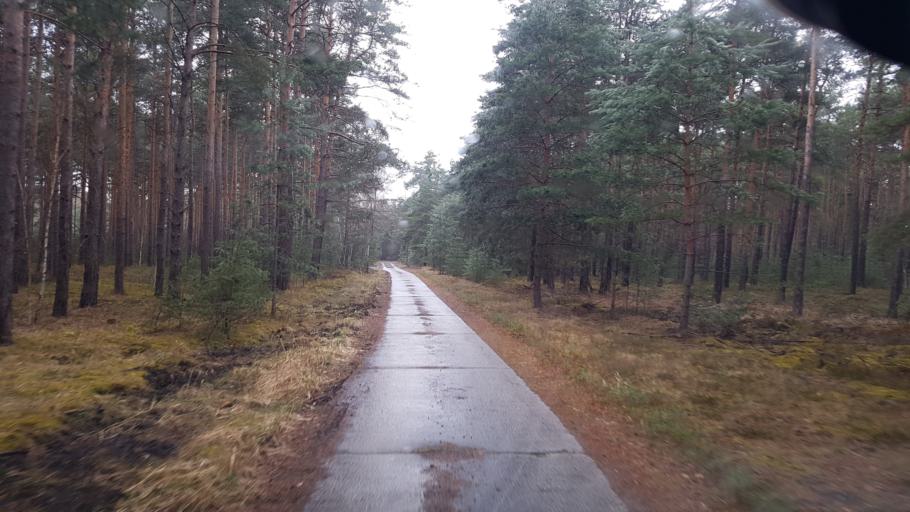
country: DE
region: Brandenburg
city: Grossraschen
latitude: 51.6146
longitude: 13.9812
